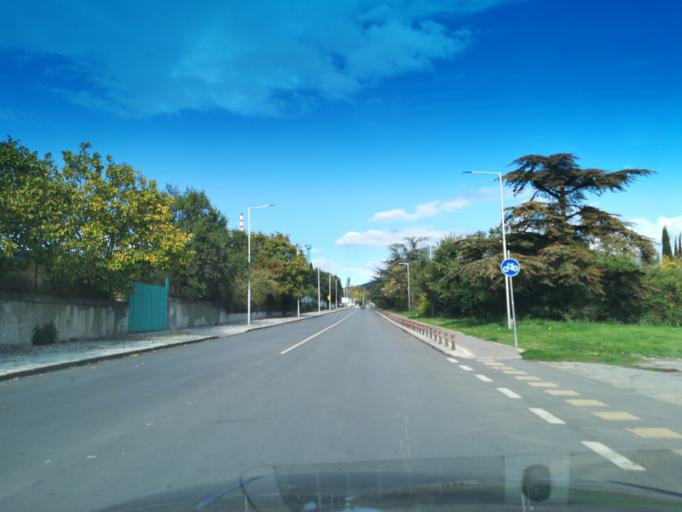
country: BG
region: Stara Zagora
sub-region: Obshtina Stara Zagora
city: Stara Zagora
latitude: 42.4402
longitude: 25.6354
